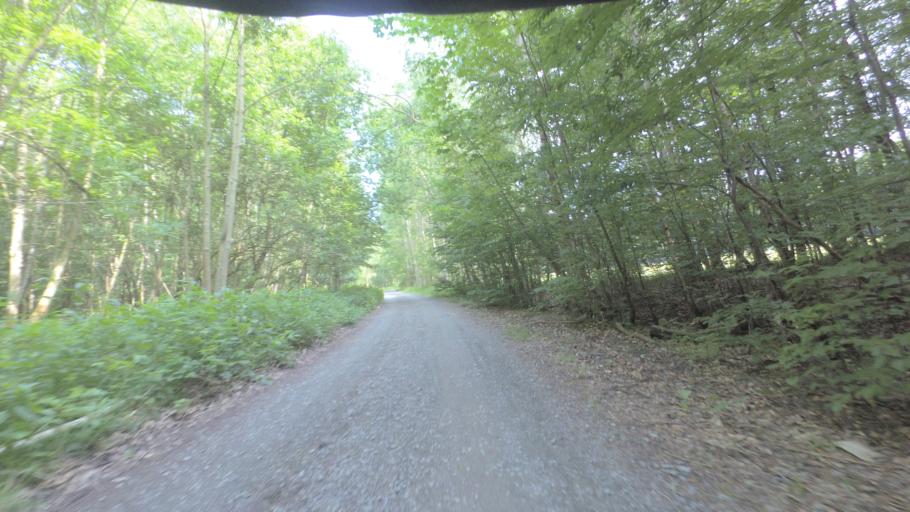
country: DE
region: Saxony-Anhalt
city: Stapelburg
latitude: 51.8833
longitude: 10.6484
